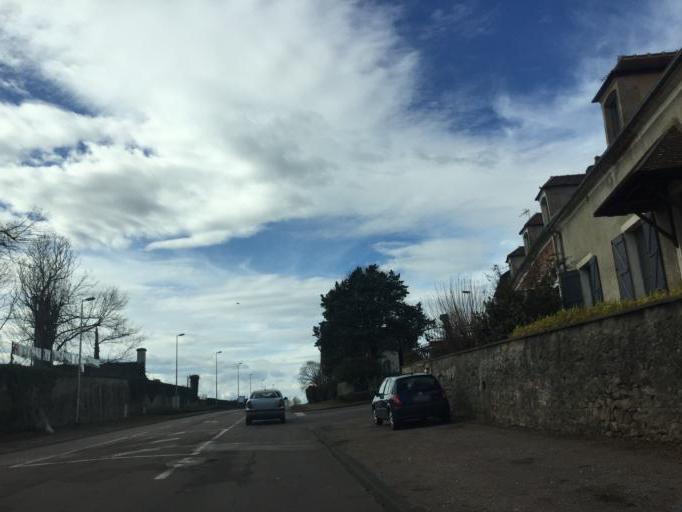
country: FR
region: Bourgogne
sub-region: Departement de l'Yonne
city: Avallon
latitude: 47.4948
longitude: 3.9029
